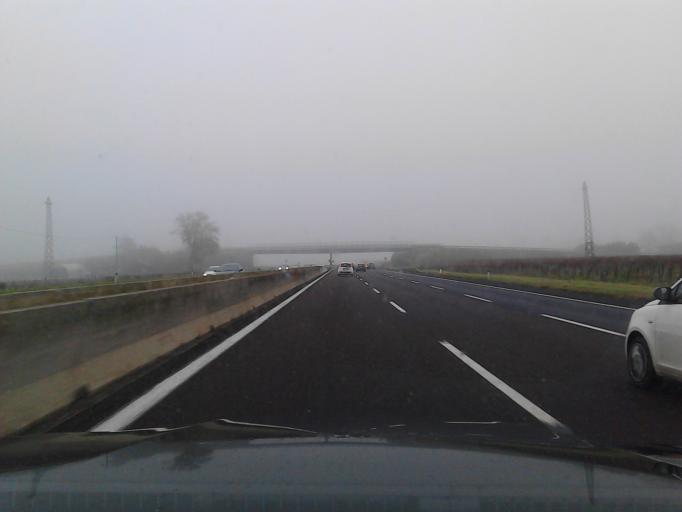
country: IT
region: Emilia-Romagna
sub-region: Provincia di Bologna
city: Castel Guelfo di Bologna
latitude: 44.4009
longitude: 11.6899
